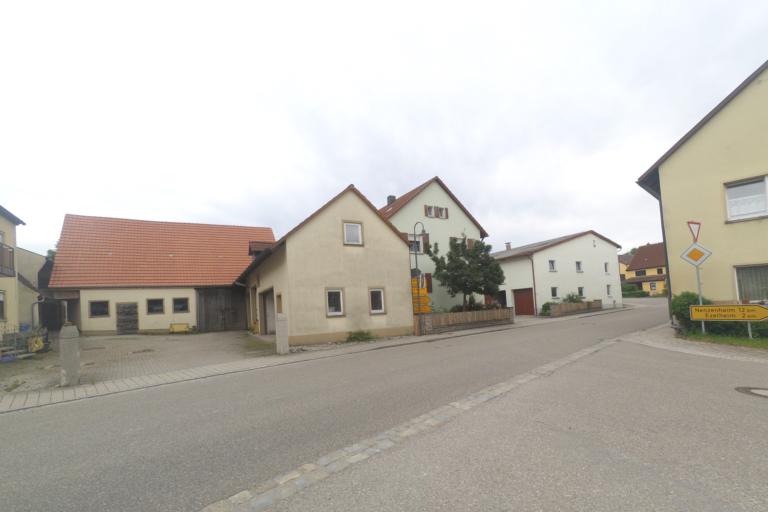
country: DE
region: Bavaria
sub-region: Regierungsbezirk Mittelfranken
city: Sugenheim
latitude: 49.5866
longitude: 10.4169
